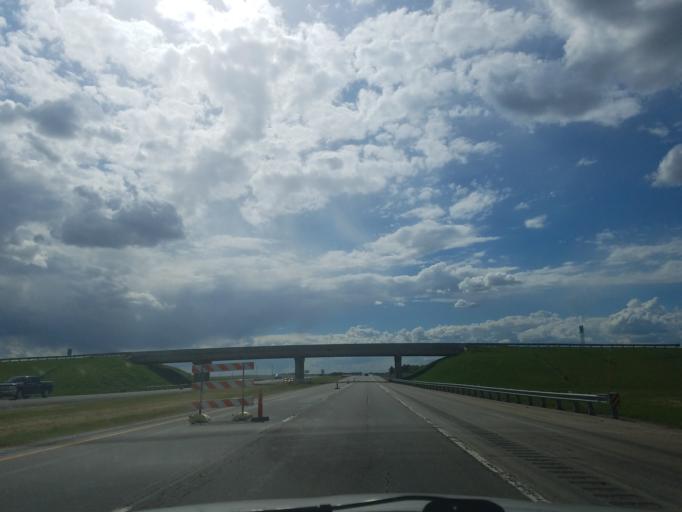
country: US
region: North Dakota
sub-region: Barnes County
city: Valley City
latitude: 46.9201
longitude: -97.7855
